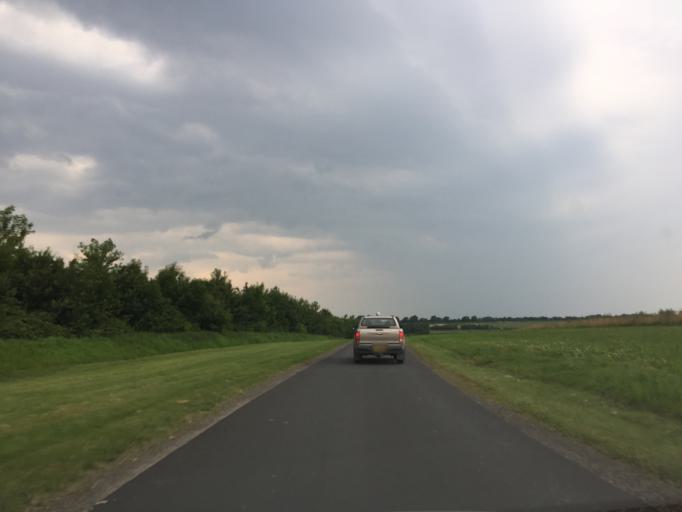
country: DK
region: Central Jutland
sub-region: Viborg Kommune
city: Bjerringbro
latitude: 56.3277
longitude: 9.6487
